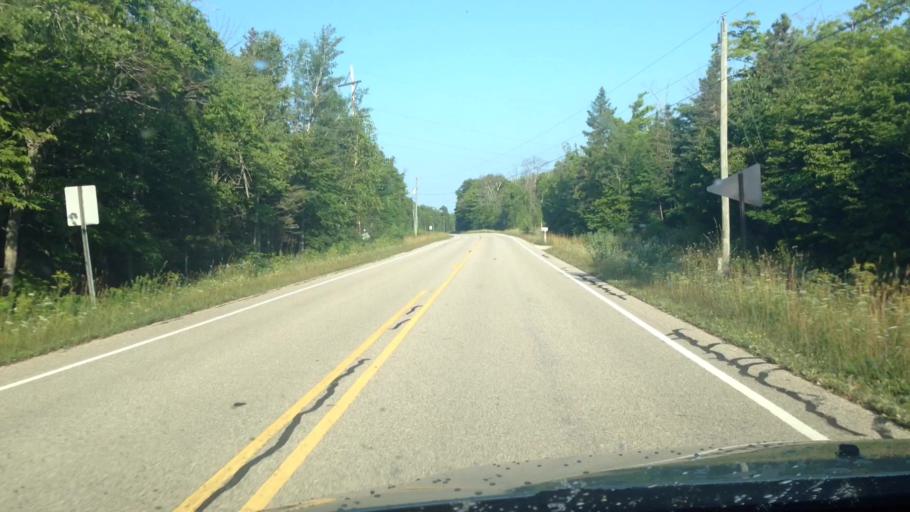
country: US
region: Michigan
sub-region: Mackinac County
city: Saint Ignace
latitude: 45.8929
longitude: -84.8001
